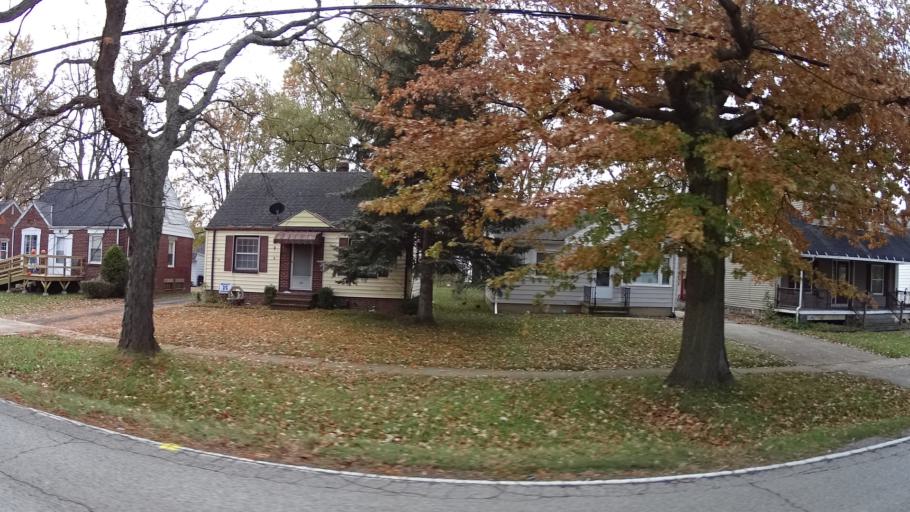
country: US
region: Ohio
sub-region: Lorain County
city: Elyria
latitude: 41.3661
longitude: -82.0851
